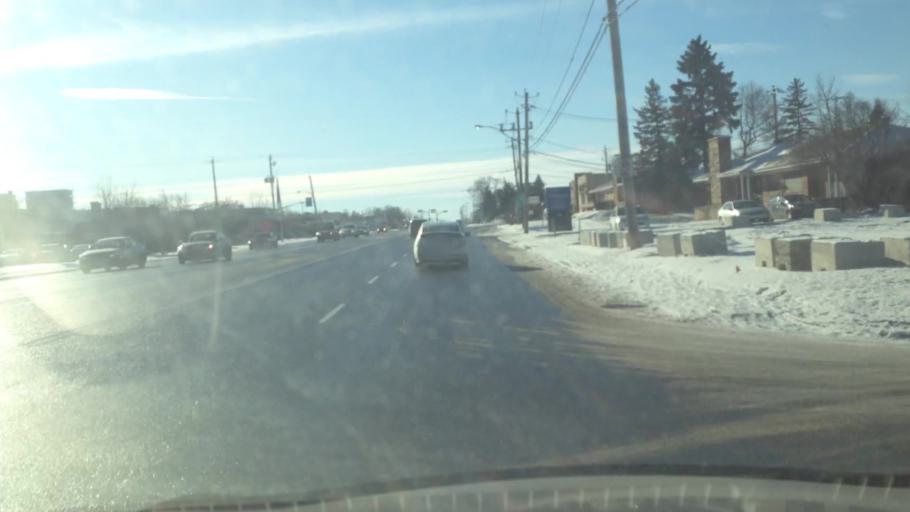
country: CA
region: Quebec
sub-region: Monteregie
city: Chateauguay
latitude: 45.3613
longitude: -73.7145
